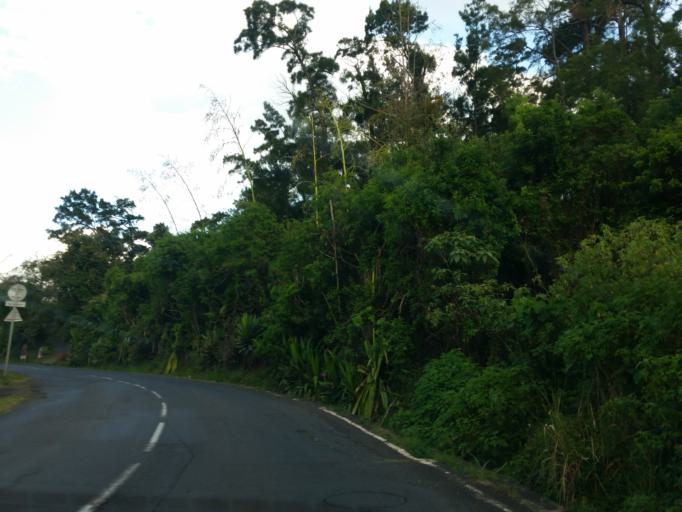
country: RE
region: Reunion
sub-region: Reunion
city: Saint-Denis
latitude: -20.8856
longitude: 55.4228
